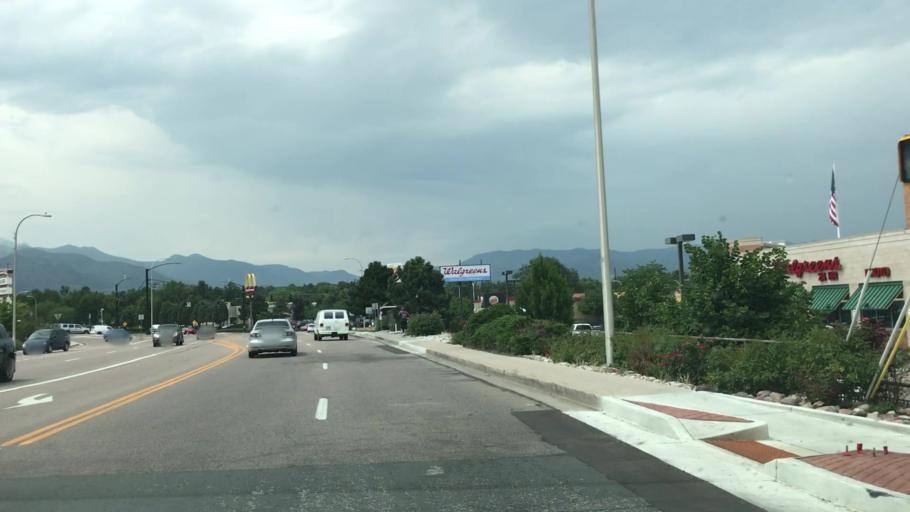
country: US
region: Colorado
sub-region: El Paso County
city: Colorado Springs
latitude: 38.8060
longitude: -104.8206
